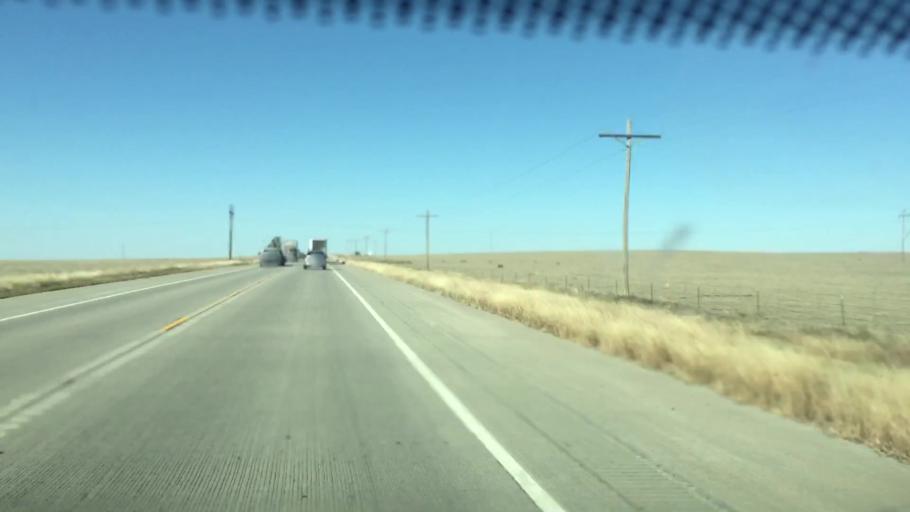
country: US
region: Colorado
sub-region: Prowers County
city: Lamar
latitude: 38.2619
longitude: -102.7239
